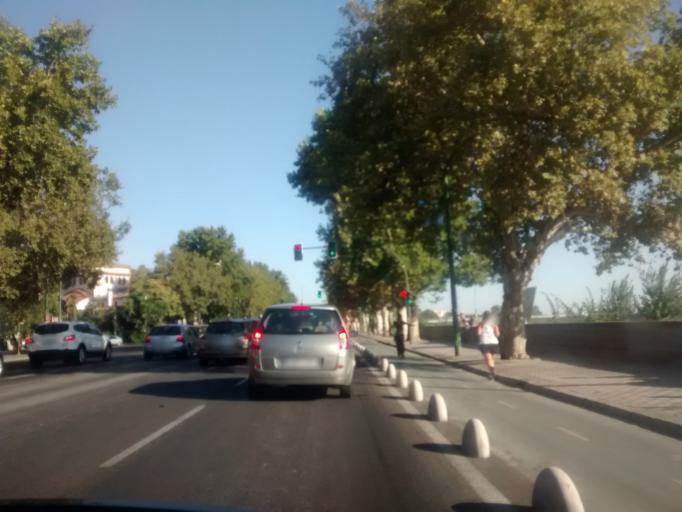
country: ES
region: Andalusia
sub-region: Provincia de Sevilla
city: Sevilla
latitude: 37.3783
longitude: -5.9933
